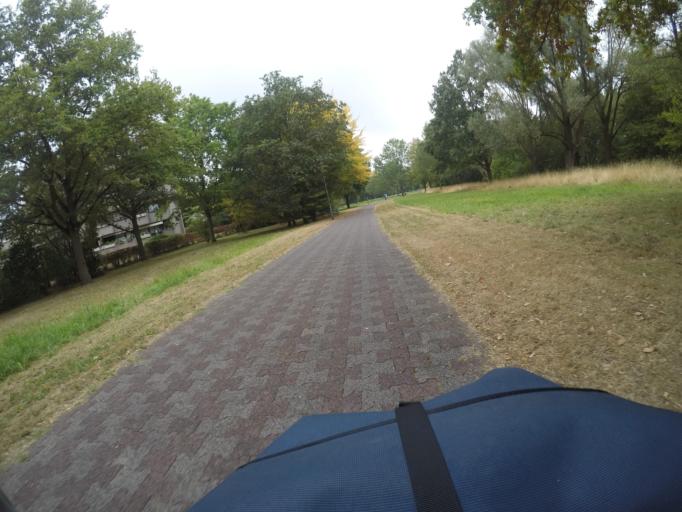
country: DE
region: North Rhine-Westphalia
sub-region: Regierungsbezirk Dusseldorf
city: Krefeld
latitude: 51.3091
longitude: 6.5940
